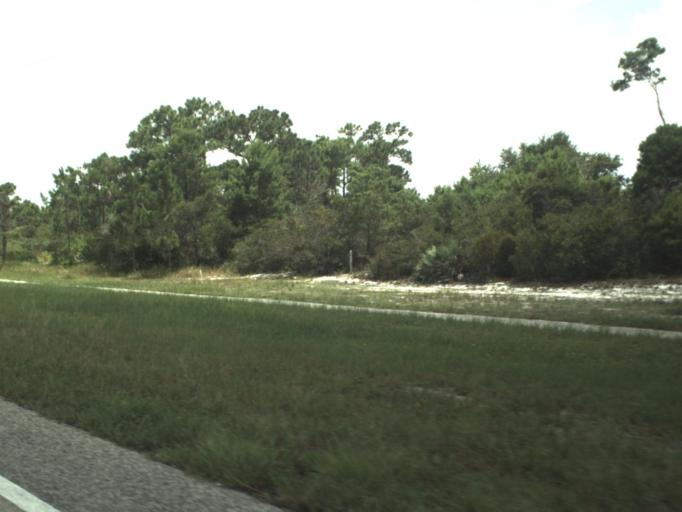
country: US
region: Florida
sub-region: Martin County
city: Hobe Sound
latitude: 27.0941
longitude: -80.1557
